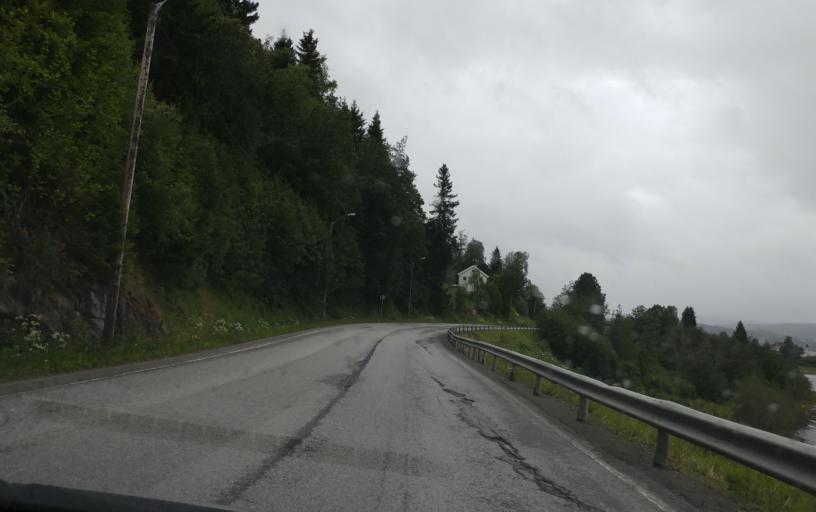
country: NO
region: Sor-Trondelag
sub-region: Selbu
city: Mebonden
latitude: 63.2382
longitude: 11.0446
